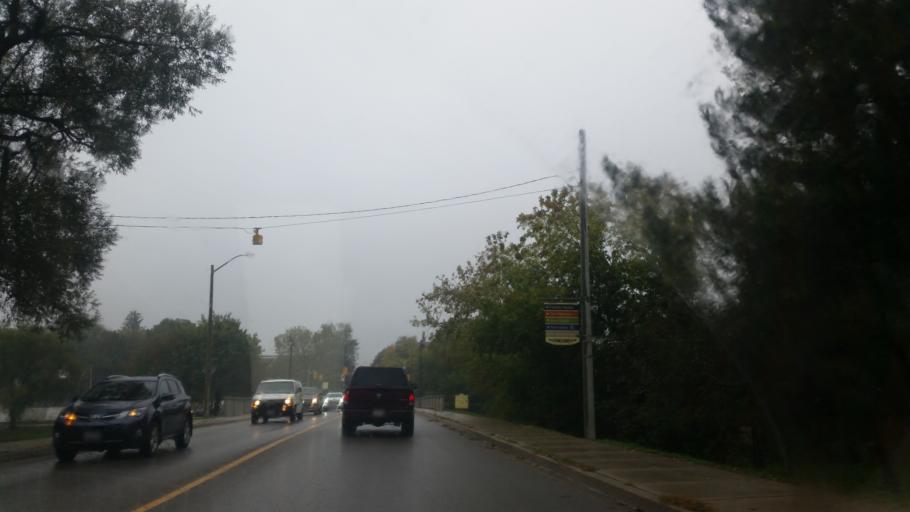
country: CA
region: Ontario
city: Stratford
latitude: 43.3745
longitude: -80.9797
